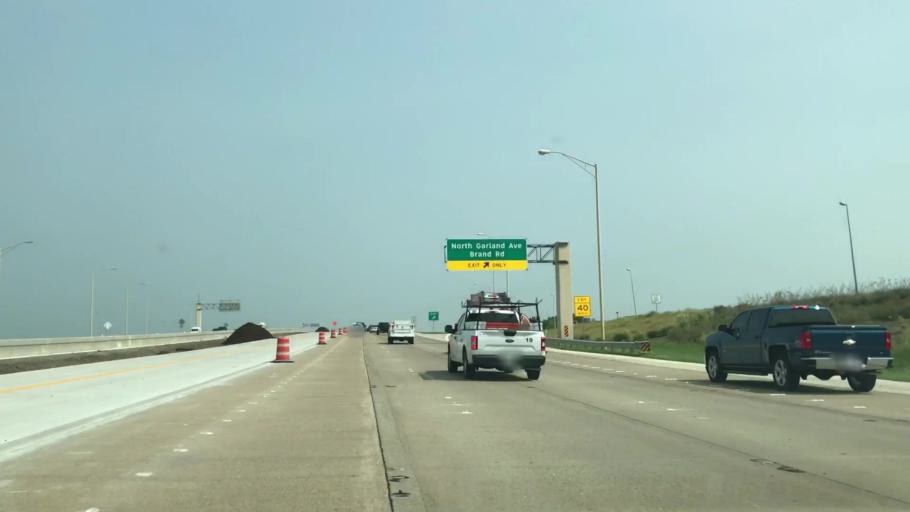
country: US
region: Texas
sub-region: Dallas County
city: Sachse
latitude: 32.9697
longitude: -96.6481
